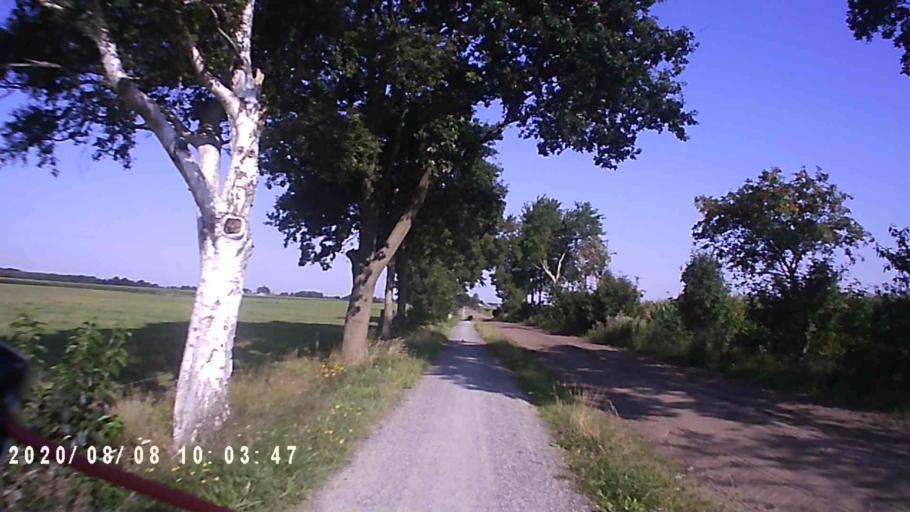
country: NL
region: Groningen
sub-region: Gemeente Leek
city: Leek
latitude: 53.1095
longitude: 6.3797
